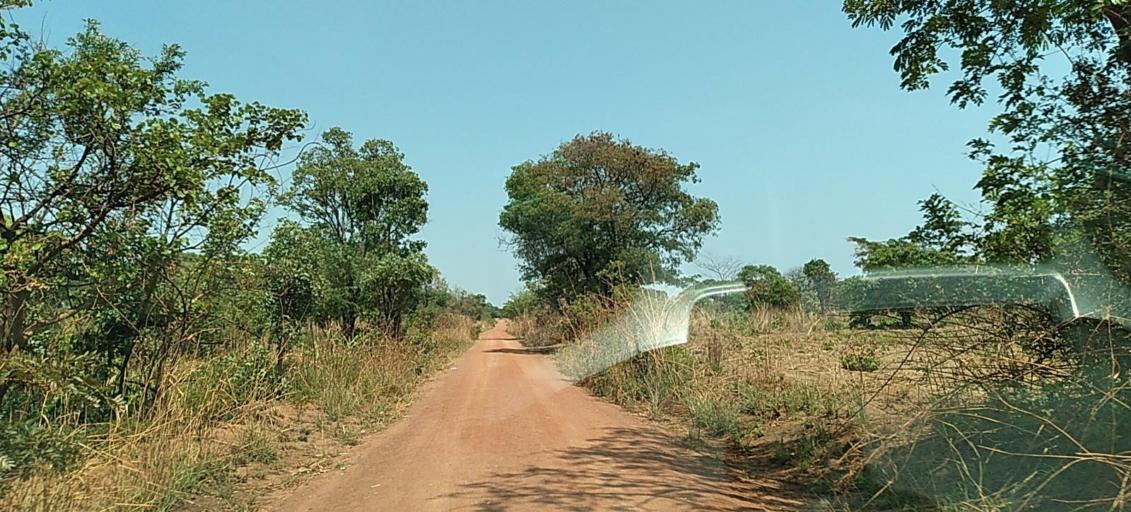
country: ZM
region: Copperbelt
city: Chingola
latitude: -12.5439
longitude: 27.7460
